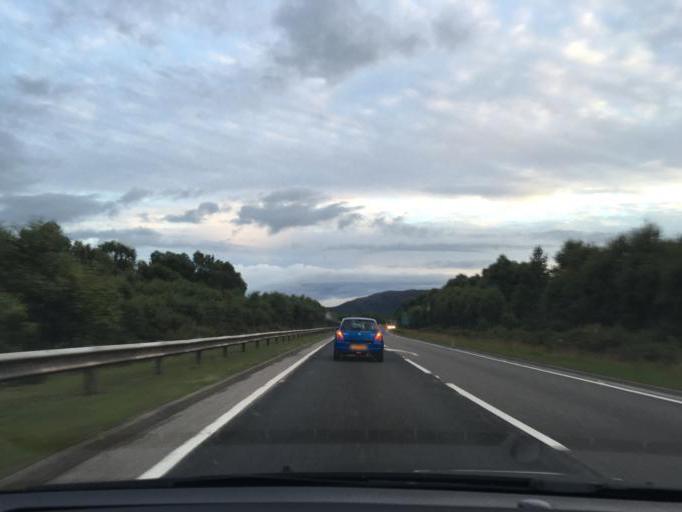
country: GB
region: Scotland
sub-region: Highland
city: Aviemore
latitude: 57.2177
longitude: -3.8222
